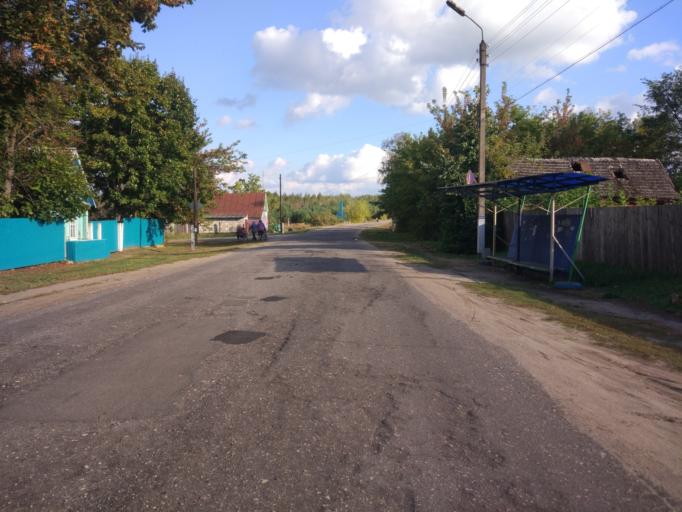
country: RU
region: Brjansk
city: Vyshkov
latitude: 52.4738
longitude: 31.6961
